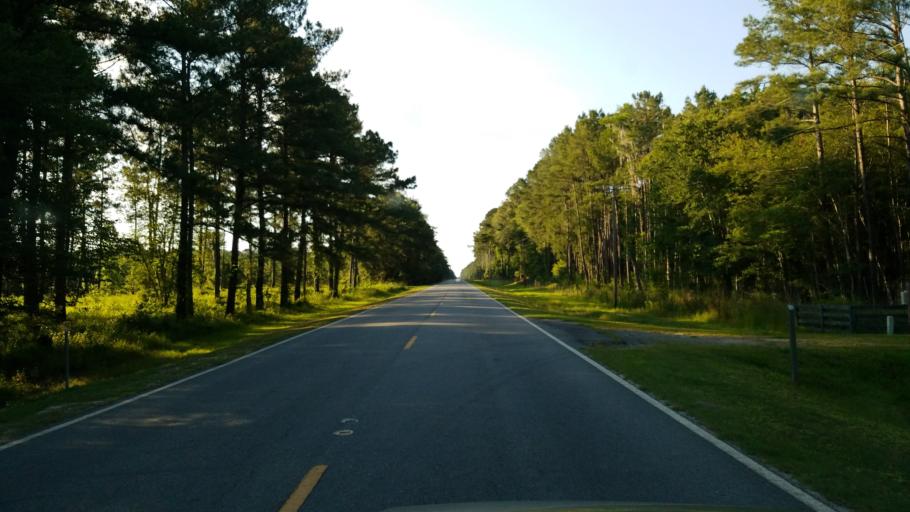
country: US
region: Georgia
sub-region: Lanier County
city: Lakeland
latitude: 31.0710
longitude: -83.0732
